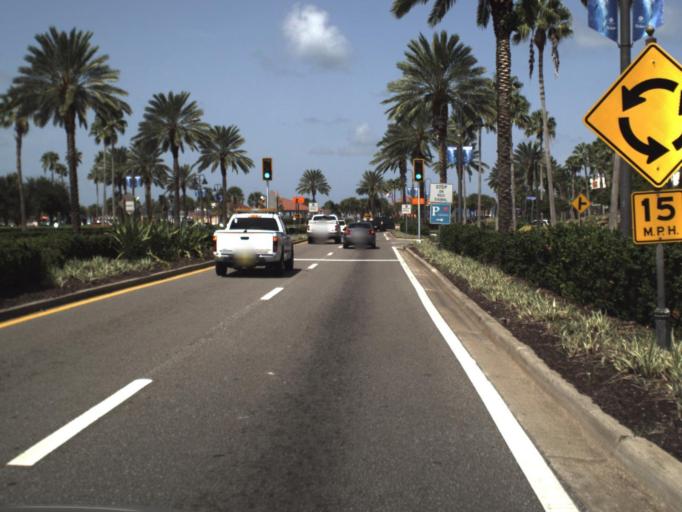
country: US
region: Florida
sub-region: Pinellas County
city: Clearwater
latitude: 27.9776
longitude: -82.8254
